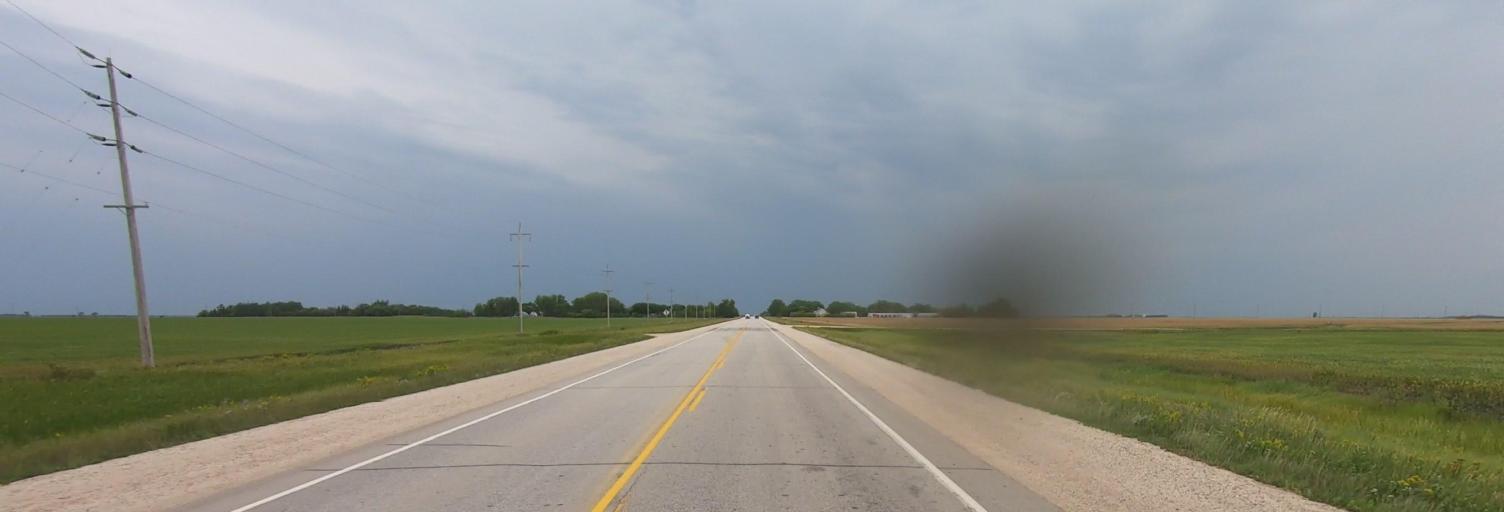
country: CA
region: Manitoba
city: Headingley
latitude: 49.7684
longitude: -97.3562
